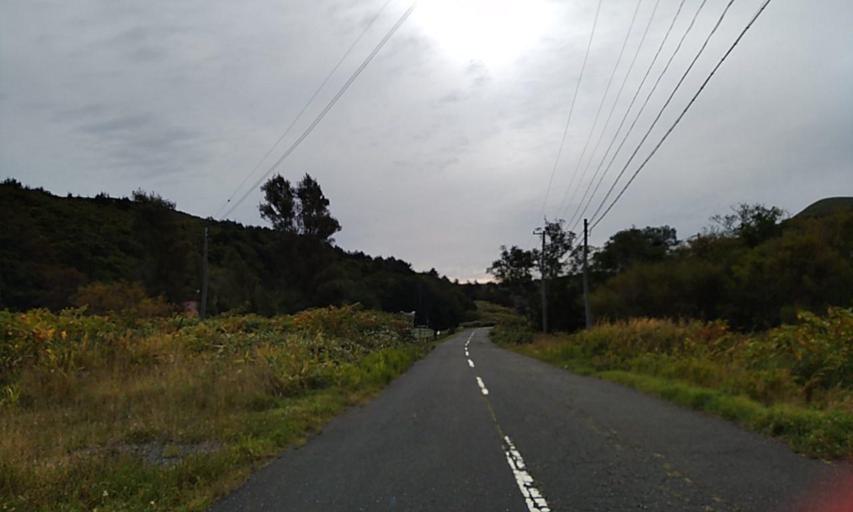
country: JP
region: Hokkaido
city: Makubetsu
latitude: 45.4860
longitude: 141.8826
